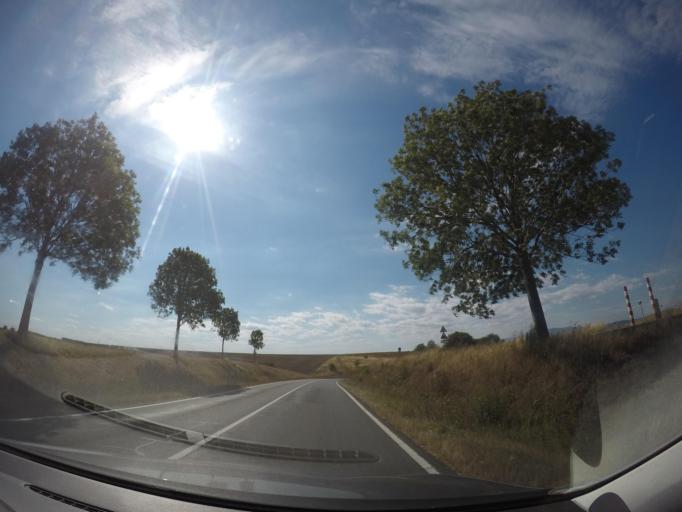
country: DE
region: Saxony-Anhalt
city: Heudeber
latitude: 51.9617
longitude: 10.8332
